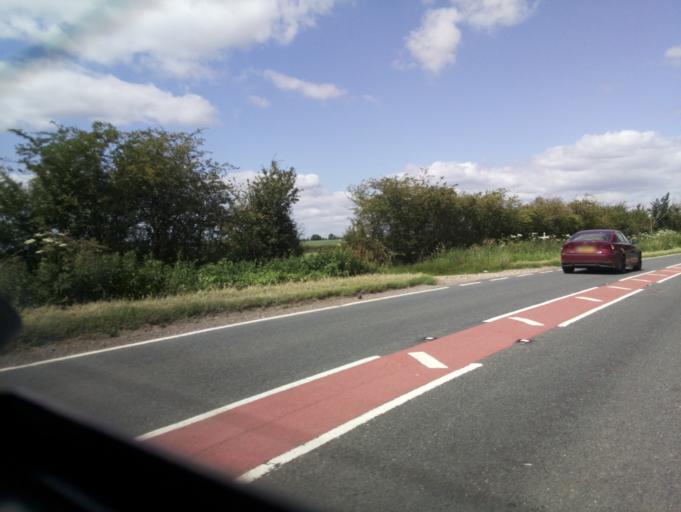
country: GB
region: England
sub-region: Buckinghamshire
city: Aylesbury
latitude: 51.8455
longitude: -0.8229
